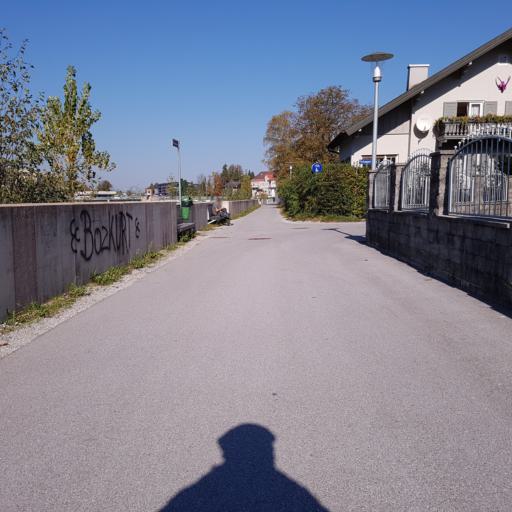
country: AT
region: Salzburg
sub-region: Politischer Bezirk Hallein
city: Hallein
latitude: 47.6802
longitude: 13.0990
